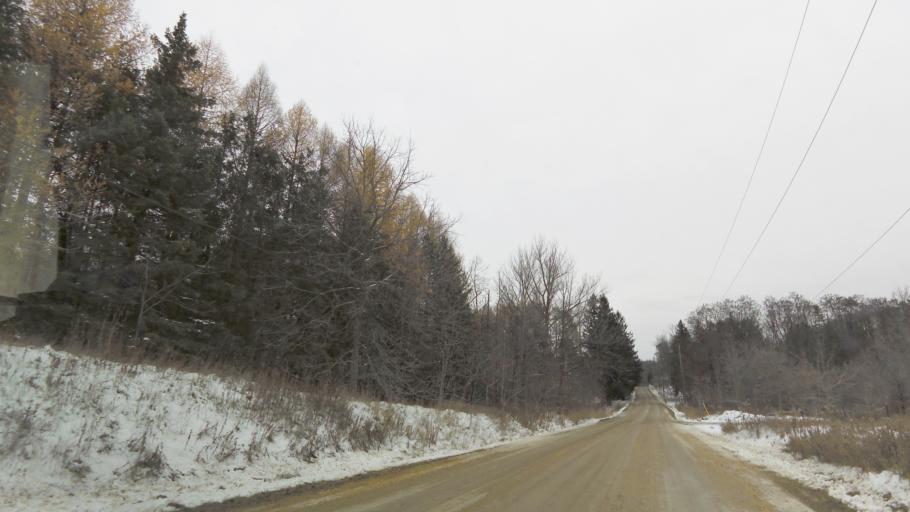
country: CA
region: Ontario
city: Vaughan
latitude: 43.9450
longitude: -79.6113
